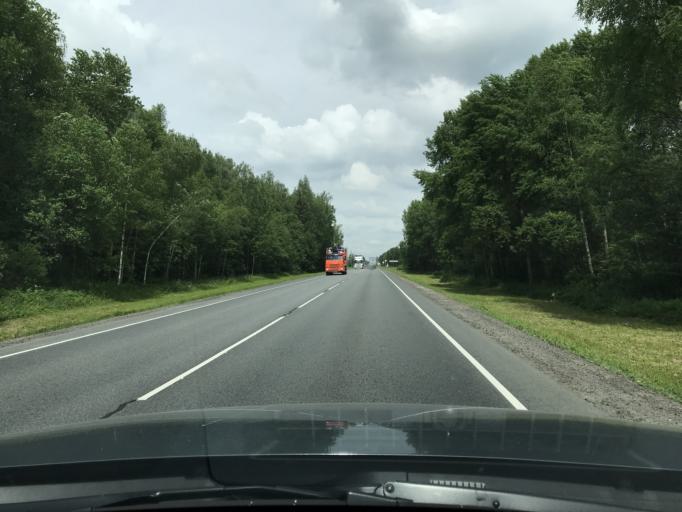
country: RU
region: Kaluga
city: Borovsk
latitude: 55.3701
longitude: 36.4120
